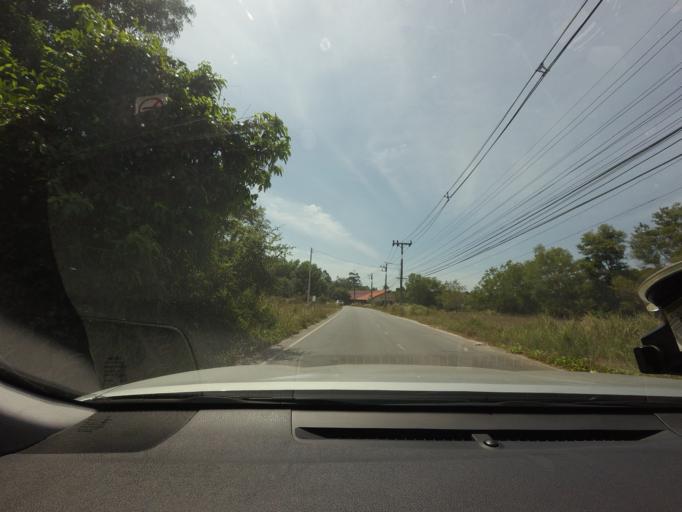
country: TH
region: Narathiwat
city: Narathiwat
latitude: 6.4445
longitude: 101.8001
